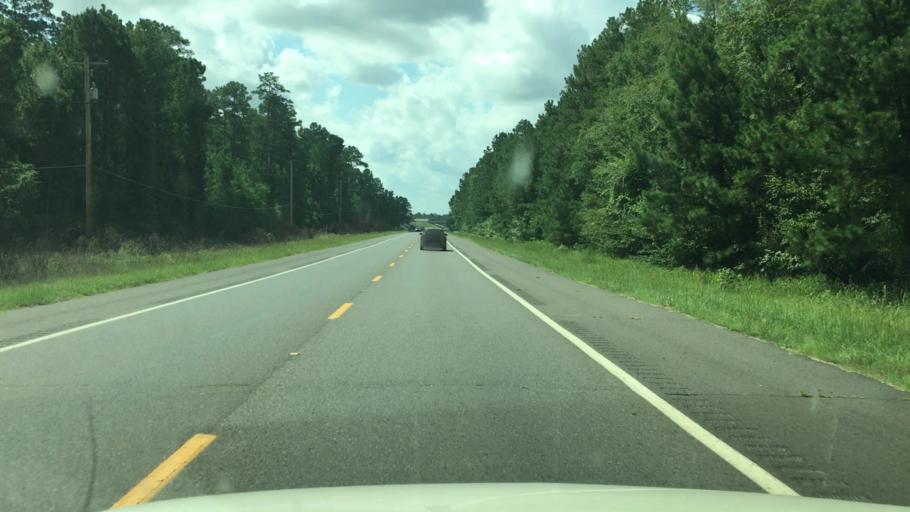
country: US
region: Arkansas
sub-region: Clark County
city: Arkadelphia
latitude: 34.1939
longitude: -93.0745
